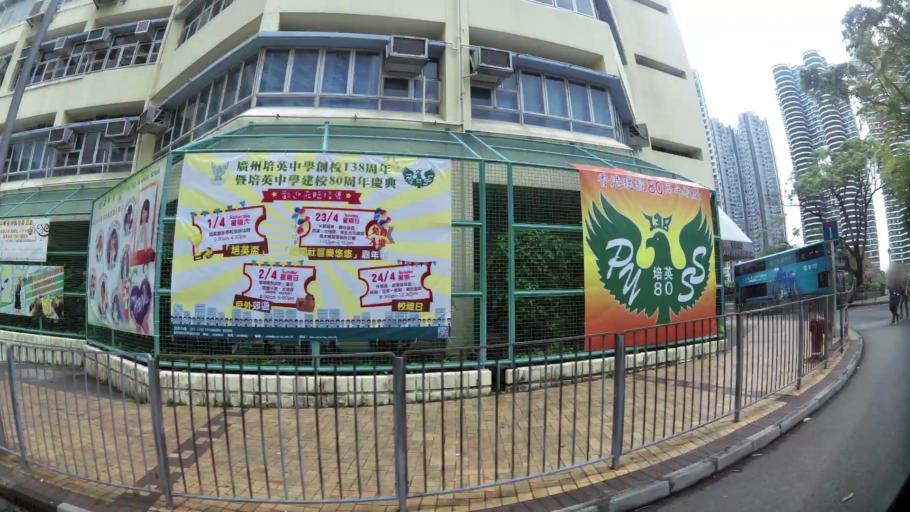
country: HK
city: Yung Shue Wan
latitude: 22.2536
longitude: 114.1356
